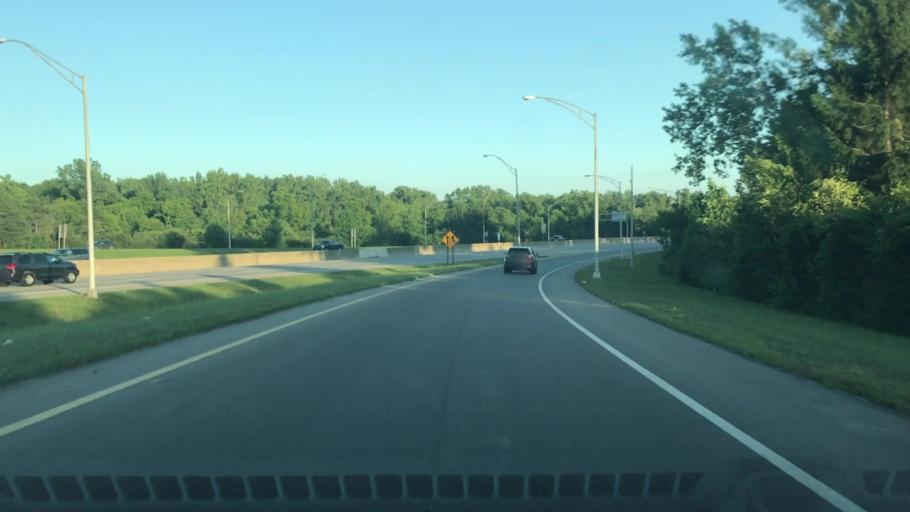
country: US
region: Ohio
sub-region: Franklin County
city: Worthington
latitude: 40.0616
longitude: -83.0318
